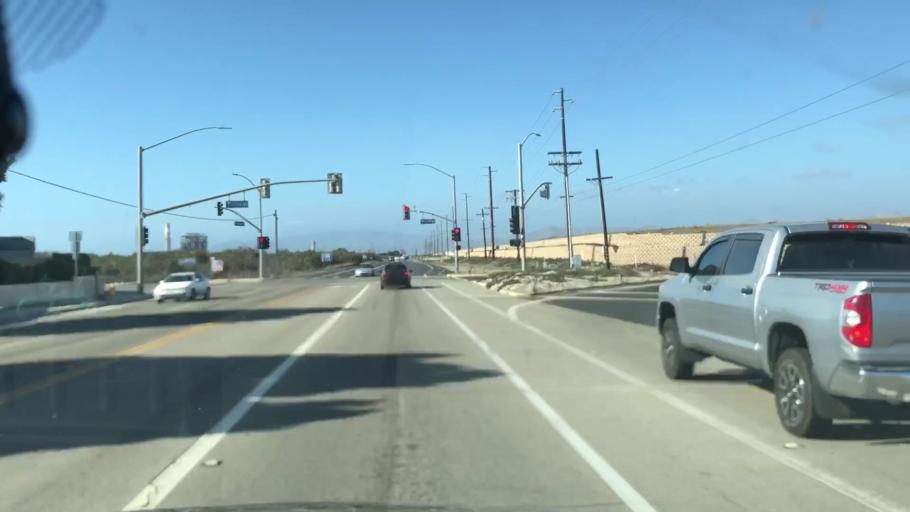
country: US
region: California
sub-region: Ventura County
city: Oxnard Shores
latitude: 34.1973
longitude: -119.2422
